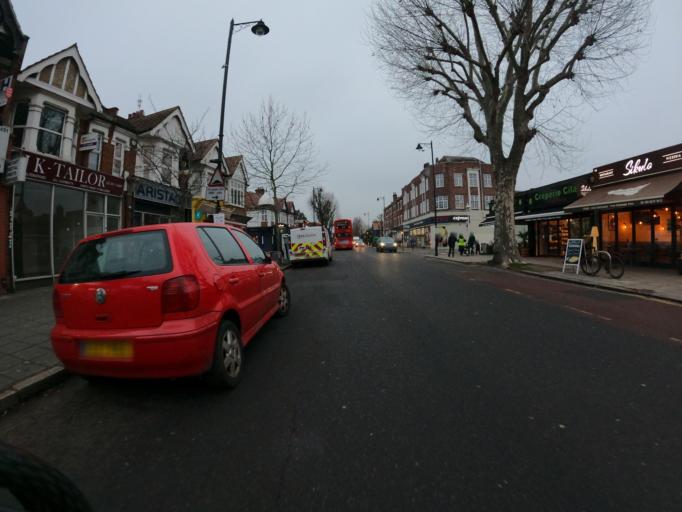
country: GB
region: England
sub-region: Greater London
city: Ealing
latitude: 51.5031
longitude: -0.3170
